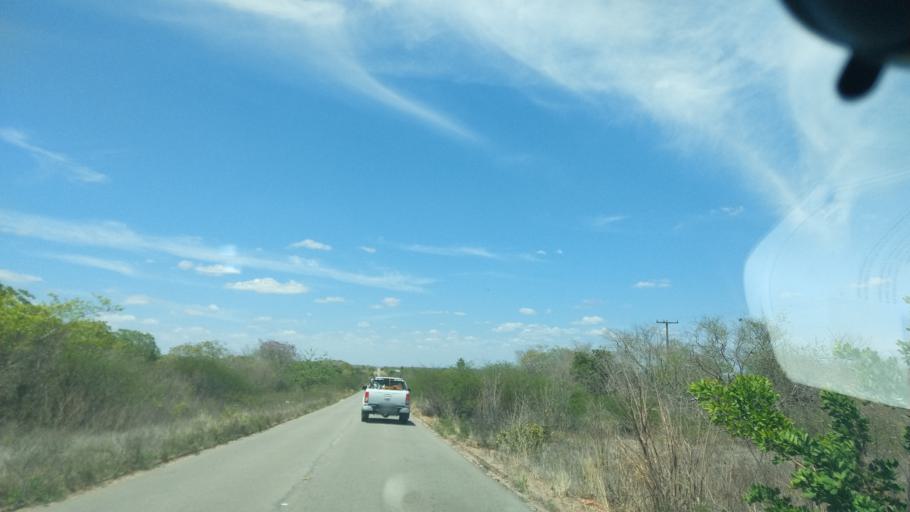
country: BR
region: Rio Grande do Norte
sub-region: Sao Paulo Do Potengi
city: Sao Paulo do Potengi
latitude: -5.9255
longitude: -35.5750
